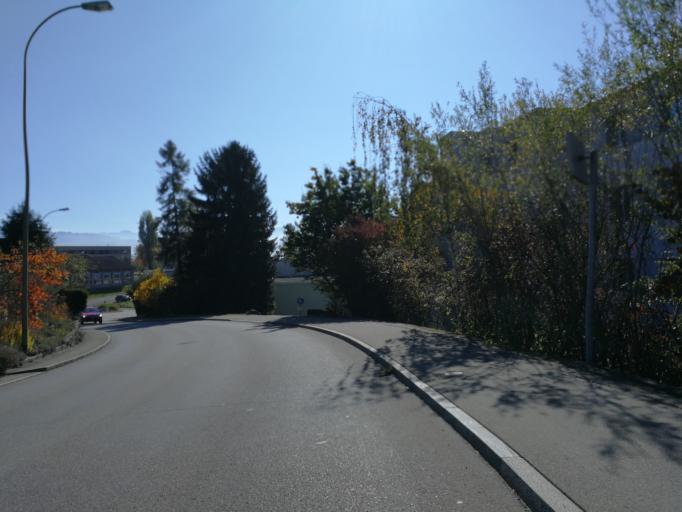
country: CH
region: Zurich
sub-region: Bezirk Meilen
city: Mannedorf
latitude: 47.2552
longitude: 8.7026
